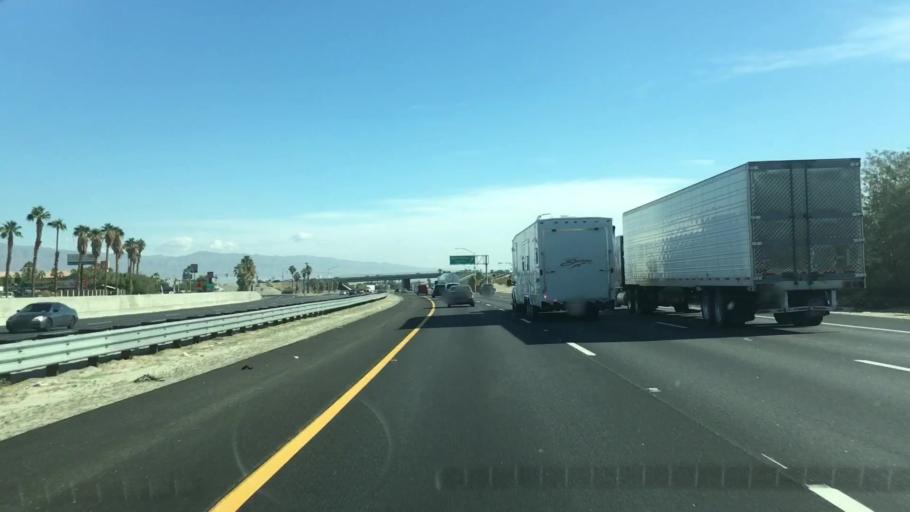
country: US
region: California
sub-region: Riverside County
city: Bermuda Dunes
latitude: 33.7616
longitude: -116.3074
